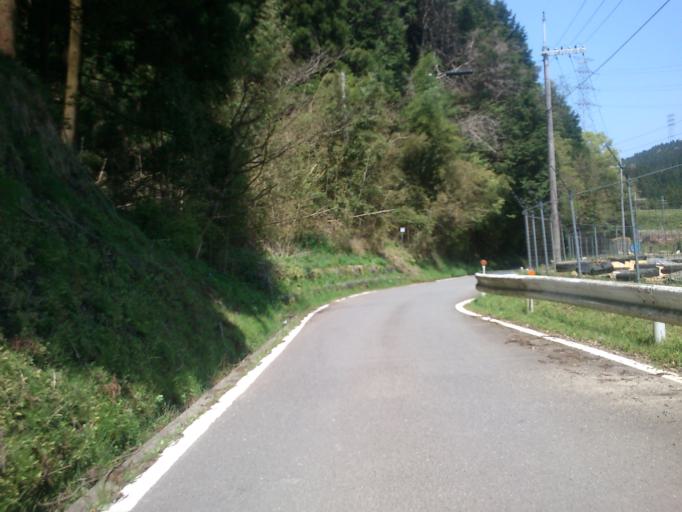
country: JP
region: Kyoto
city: Kameoka
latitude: 34.9630
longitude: 135.6242
